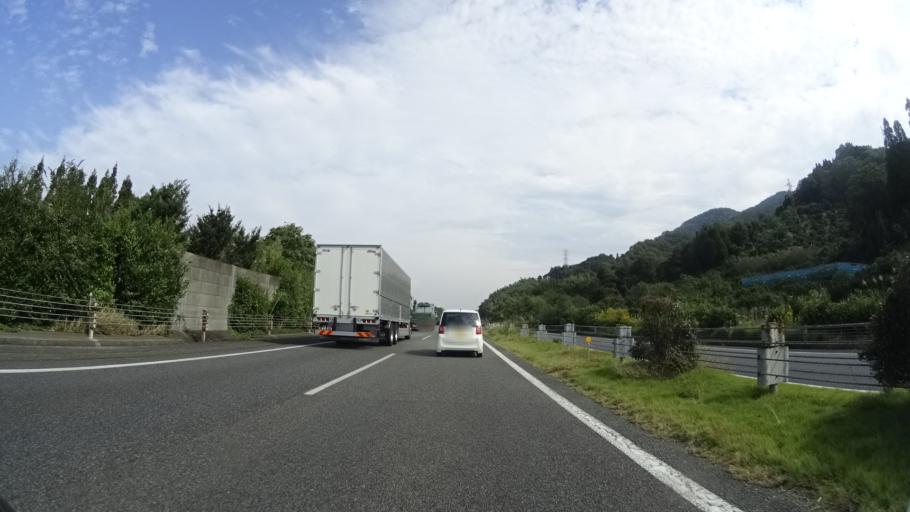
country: JP
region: Kumamoto
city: Yatsushiro
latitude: 32.5277
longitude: 130.6650
